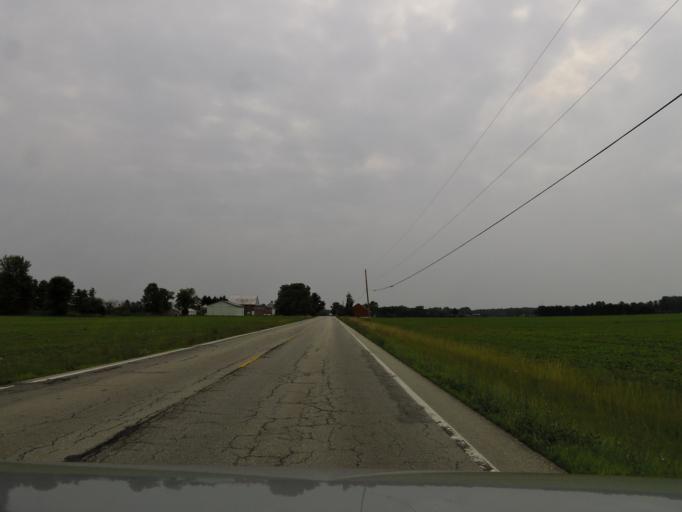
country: US
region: Ohio
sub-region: Clinton County
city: Blanchester
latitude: 39.3185
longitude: -83.9040
